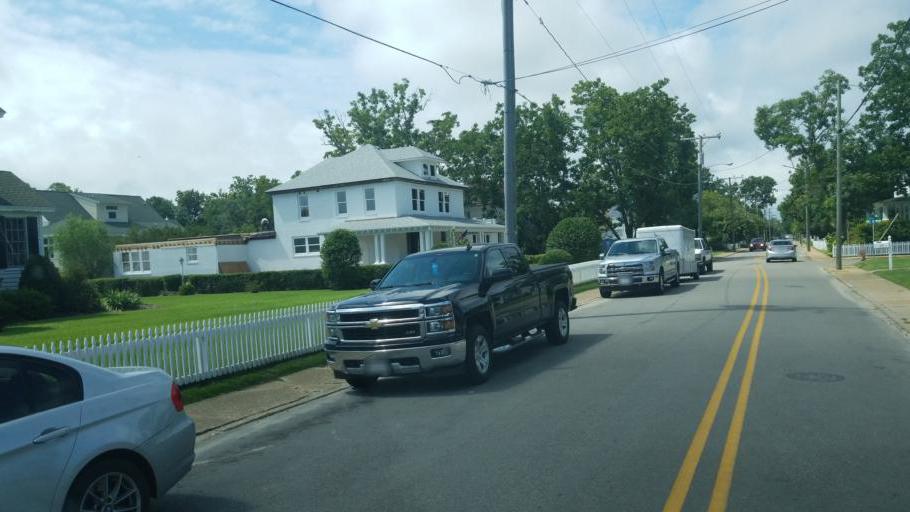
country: US
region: North Carolina
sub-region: Dare County
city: Manteo
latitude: 35.9089
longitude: -75.6709
